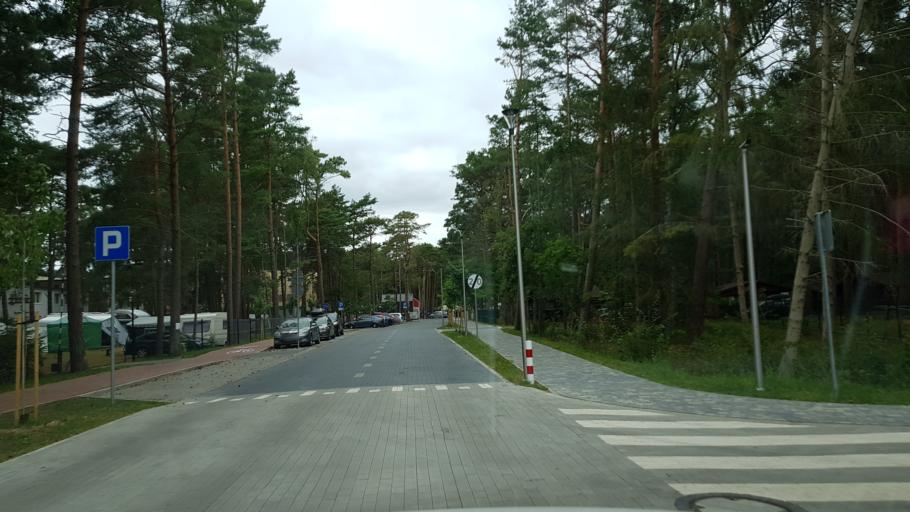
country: PL
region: West Pomeranian Voivodeship
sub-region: Powiat kamienski
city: Dziwnow
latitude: 54.0031
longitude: 14.6854
